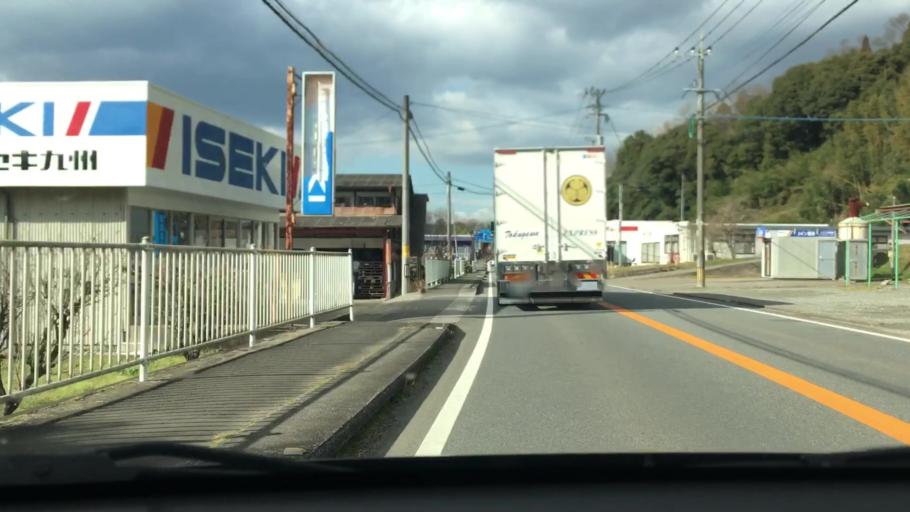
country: JP
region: Oita
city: Usuki
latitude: 33.0482
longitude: 131.6908
